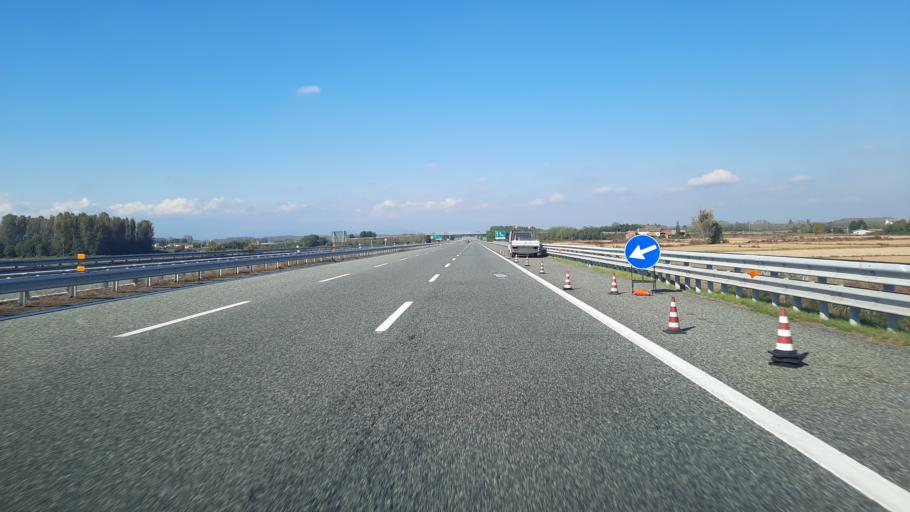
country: IT
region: Piedmont
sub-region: Provincia di Novara
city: Vicolungo
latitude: 45.4762
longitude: 8.4466
